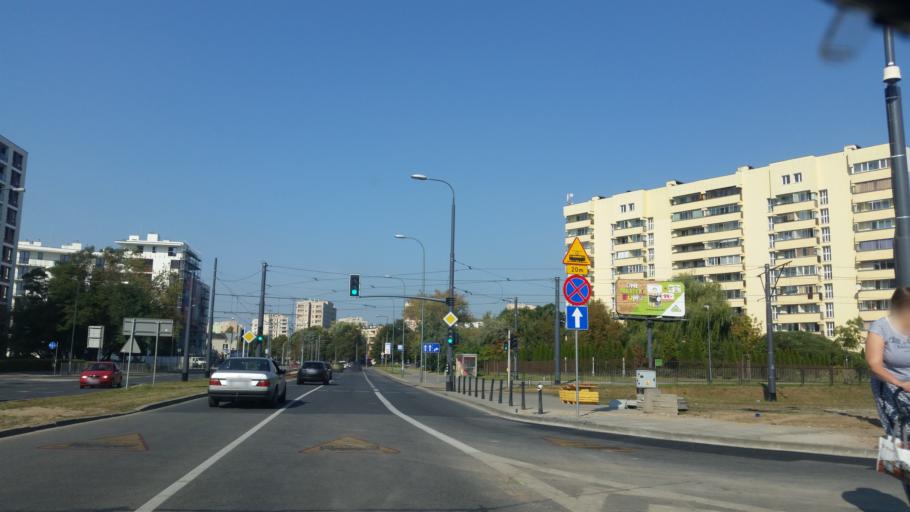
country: PL
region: Masovian Voivodeship
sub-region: Warszawa
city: Bemowo
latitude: 52.2205
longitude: 20.9167
